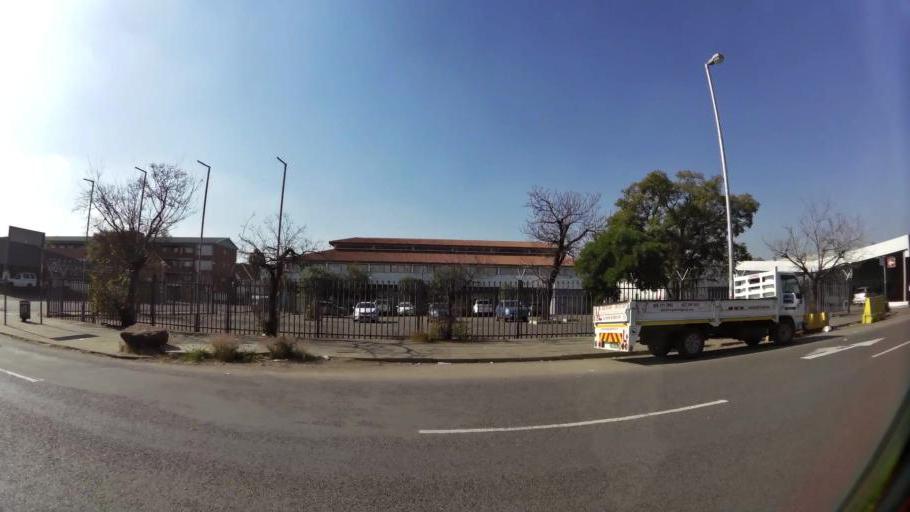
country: ZA
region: North-West
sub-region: Bojanala Platinum District Municipality
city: Rustenburg
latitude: -25.6697
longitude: 27.2460
